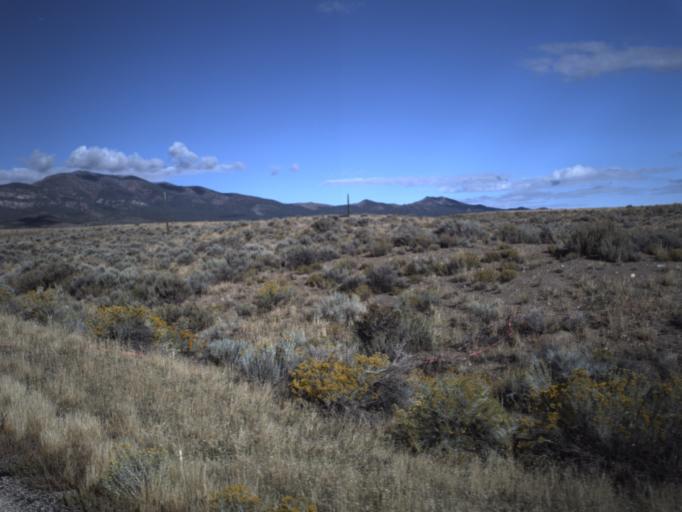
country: US
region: Utah
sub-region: Beaver County
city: Milford
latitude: 38.4462
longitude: -113.1839
